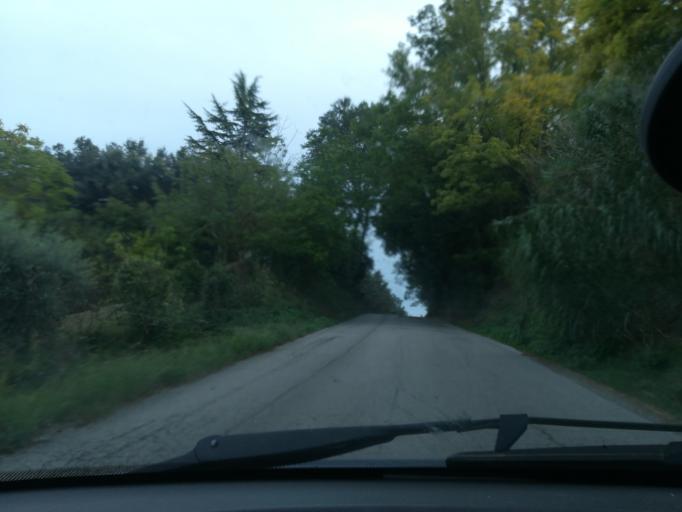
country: IT
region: The Marches
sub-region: Provincia di Macerata
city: Macerata
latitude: 43.3037
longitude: 13.4785
